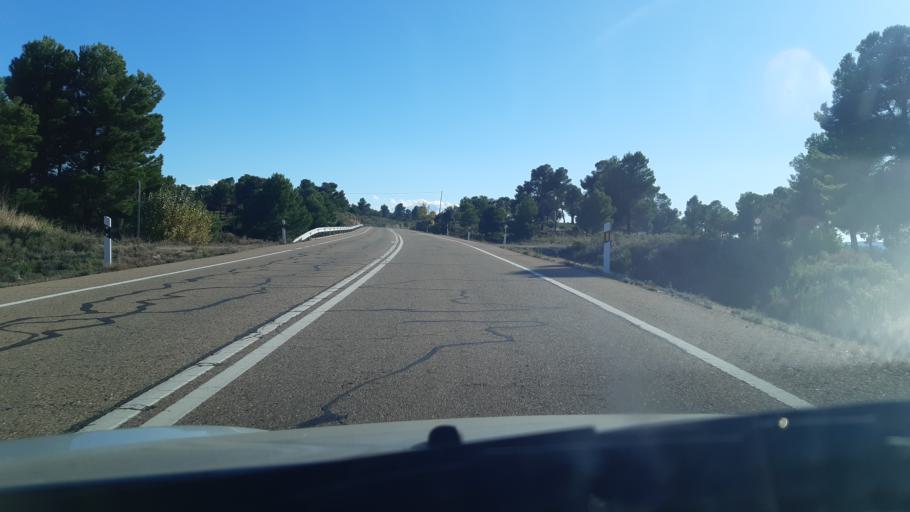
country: ES
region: Aragon
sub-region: Provincia de Teruel
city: Fornoles
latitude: 40.9333
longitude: -0.0124
